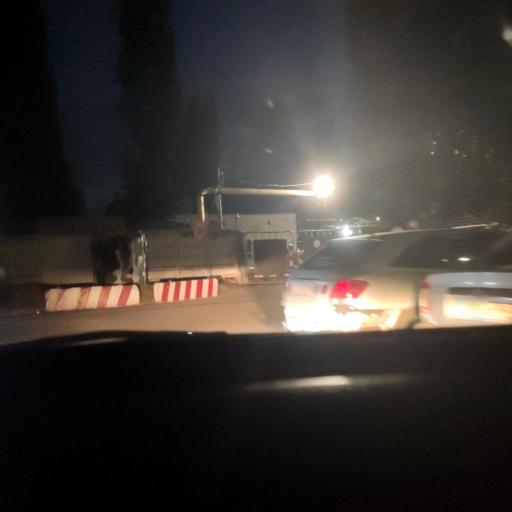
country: RU
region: Voronezj
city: Voronezh
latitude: 51.6365
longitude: 39.1825
